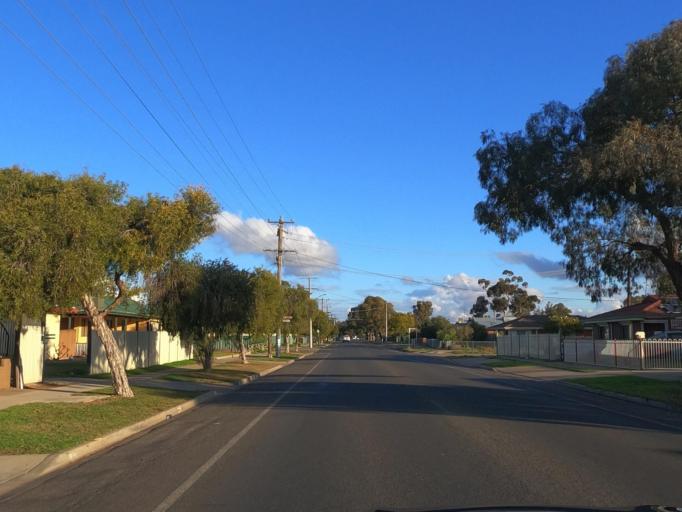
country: AU
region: Victoria
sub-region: Swan Hill
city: Swan Hill
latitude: -35.3427
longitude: 143.5438
